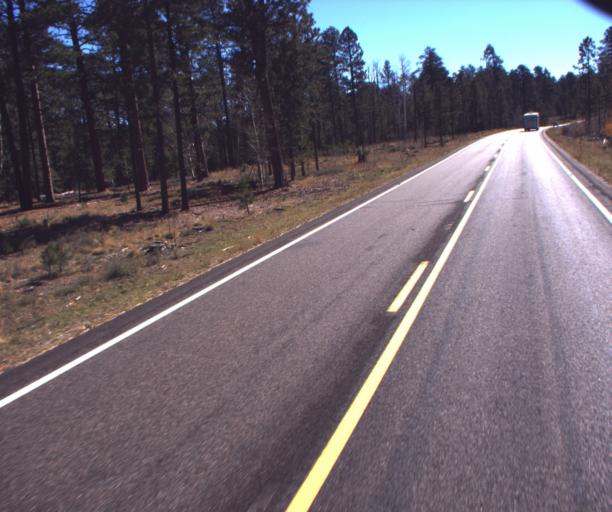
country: US
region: Arizona
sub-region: Coconino County
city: Fredonia
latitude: 36.6533
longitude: -112.1853
